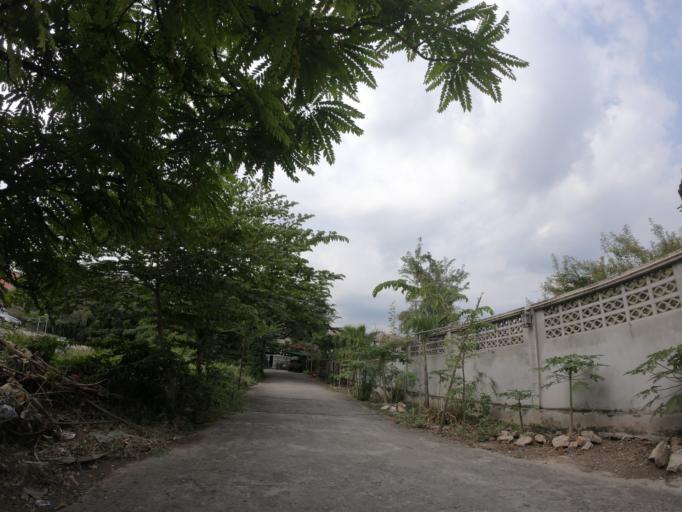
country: TH
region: Chiang Mai
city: Chiang Mai
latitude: 18.7739
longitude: 98.9845
